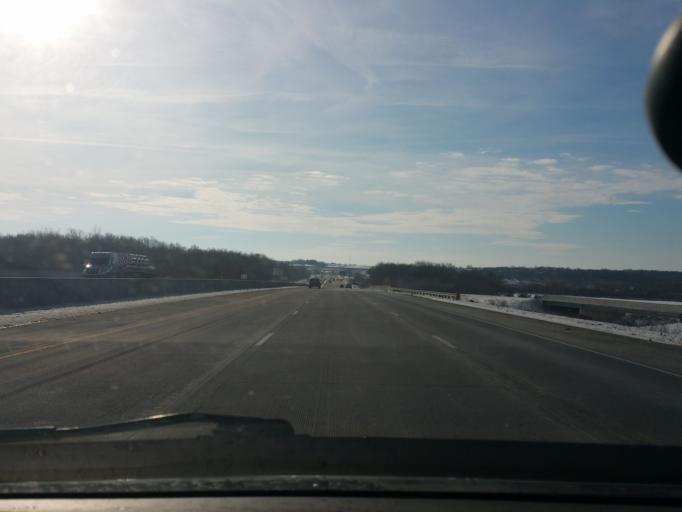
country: US
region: Iowa
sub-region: Polk County
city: West Des Moines
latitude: 41.5402
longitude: -93.7753
